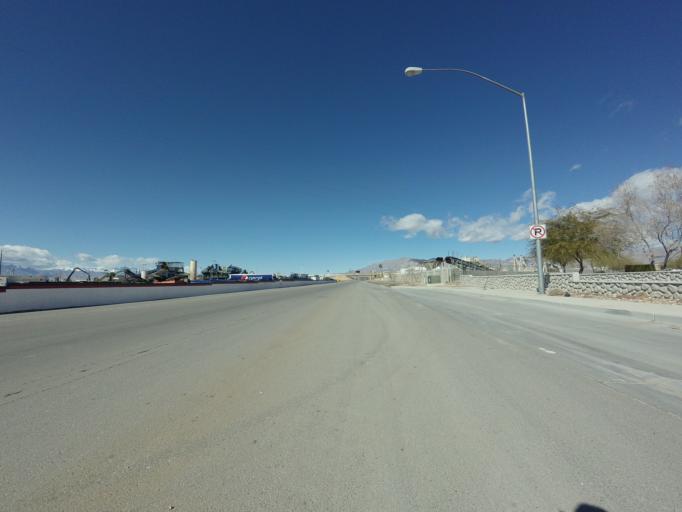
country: US
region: Nevada
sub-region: Clark County
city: Nellis Air Force Base
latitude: 36.2661
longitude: -115.0569
